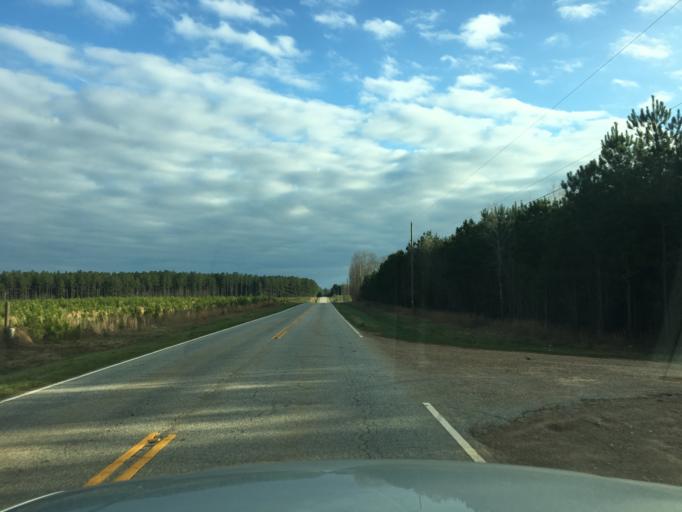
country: US
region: South Carolina
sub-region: Saluda County
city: Saluda
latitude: 34.1082
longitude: -81.8304
